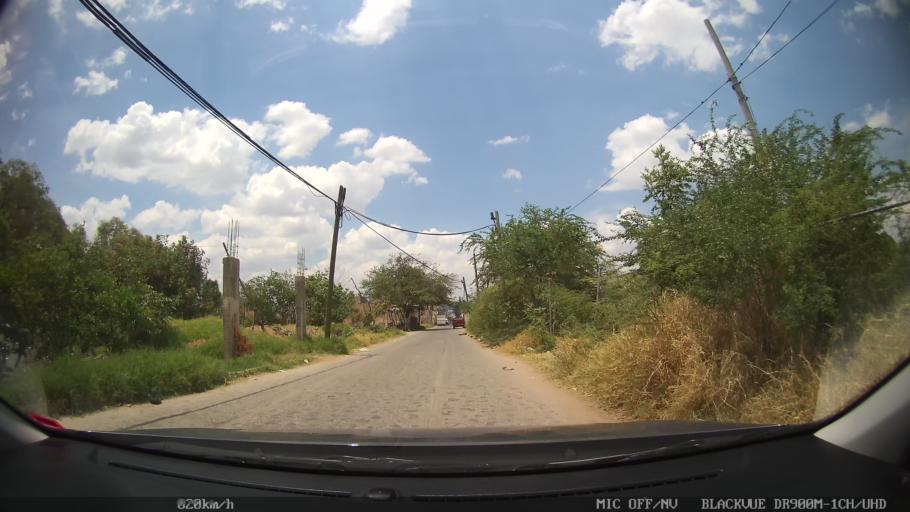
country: MX
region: Jalisco
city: Tonala
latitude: 20.6647
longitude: -103.2285
